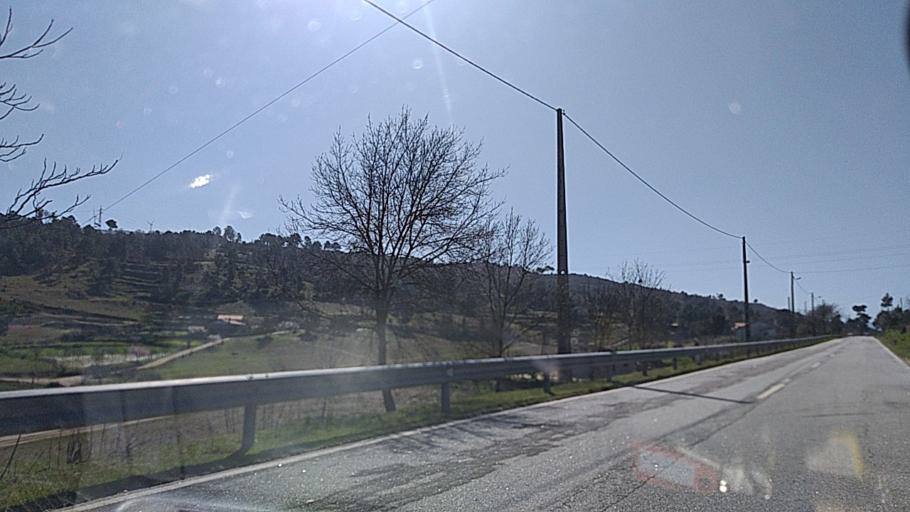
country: PT
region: Guarda
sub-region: Celorico da Beira
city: Celorico da Beira
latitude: 40.6116
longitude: -7.4151
